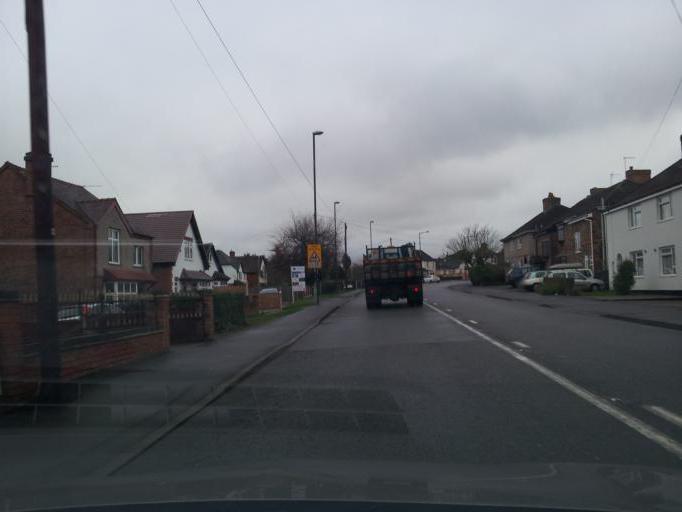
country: GB
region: England
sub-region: Derbyshire
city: Swadlincote
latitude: 52.7772
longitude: -1.5397
